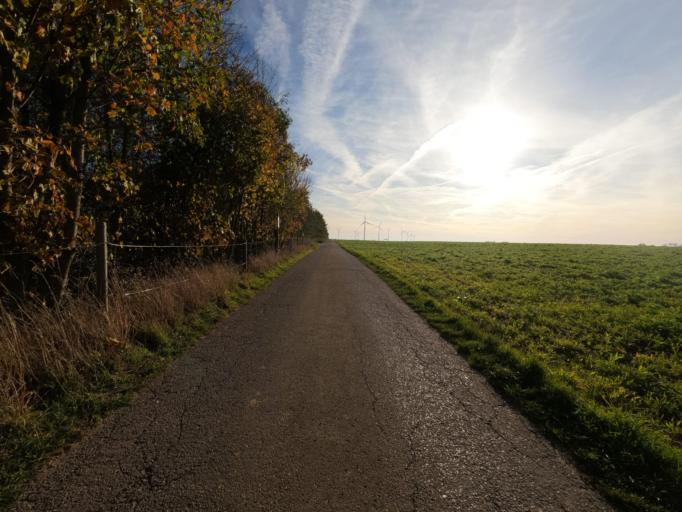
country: DE
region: North Rhine-Westphalia
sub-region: Regierungsbezirk Koln
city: Titz
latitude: 51.0409
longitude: 6.4643
